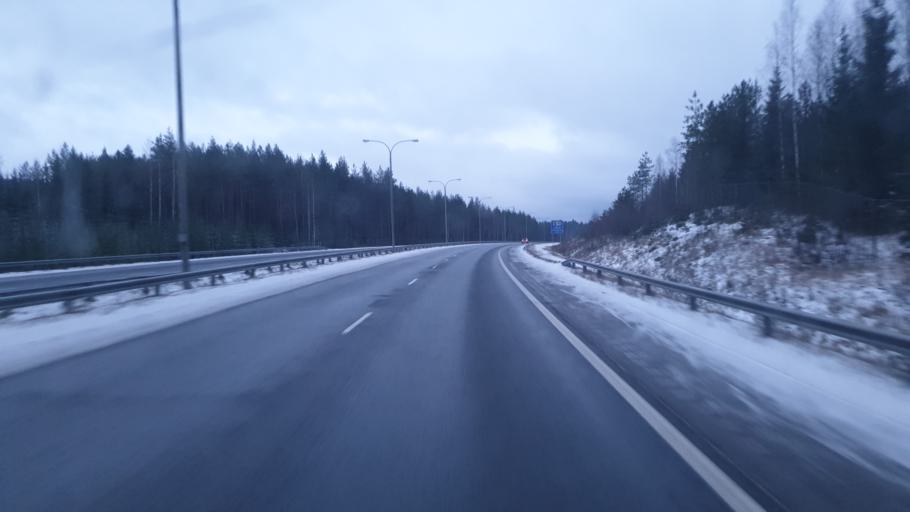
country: FI
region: Northern Savo
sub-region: Kuopio
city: Siilinjaervi
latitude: 63.0103
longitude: 27.6782
